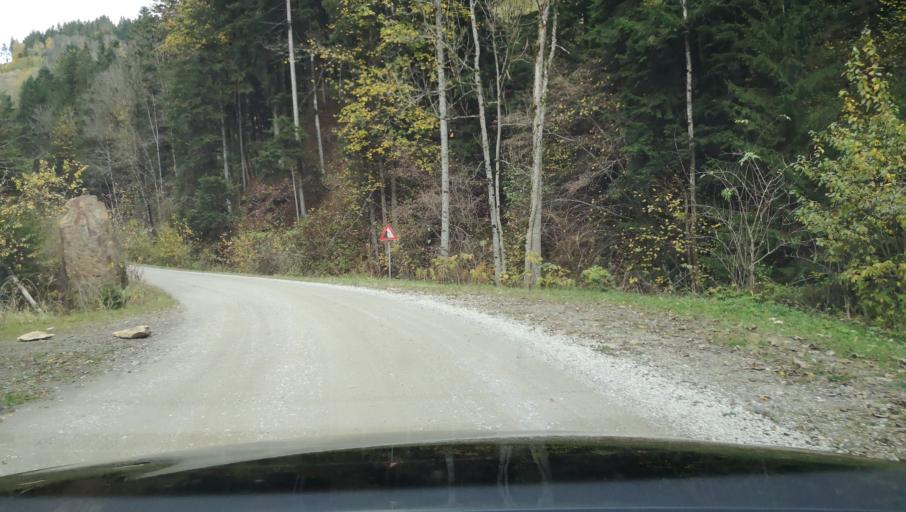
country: AT
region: Styria
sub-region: Politischer Bezirk Weiz
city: Birkfeld
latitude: 47.3753
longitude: 15.6282
